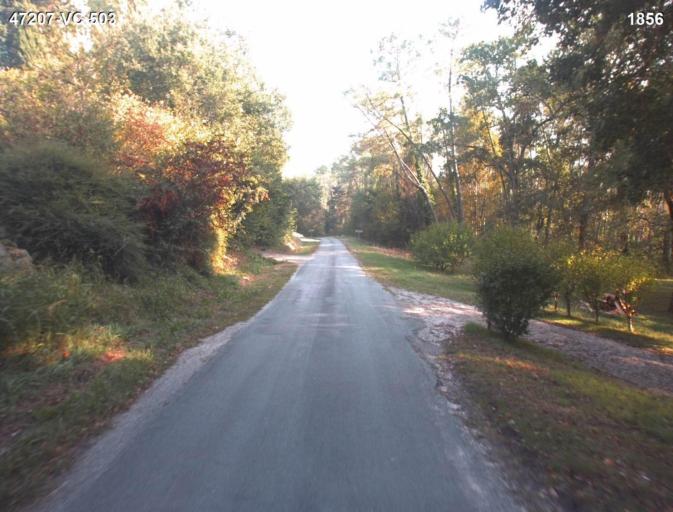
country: FR
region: Aquitaine
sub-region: Departement du Lot-et-Garonne
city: Barbaste
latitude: 44.1909
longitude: 0.2300
